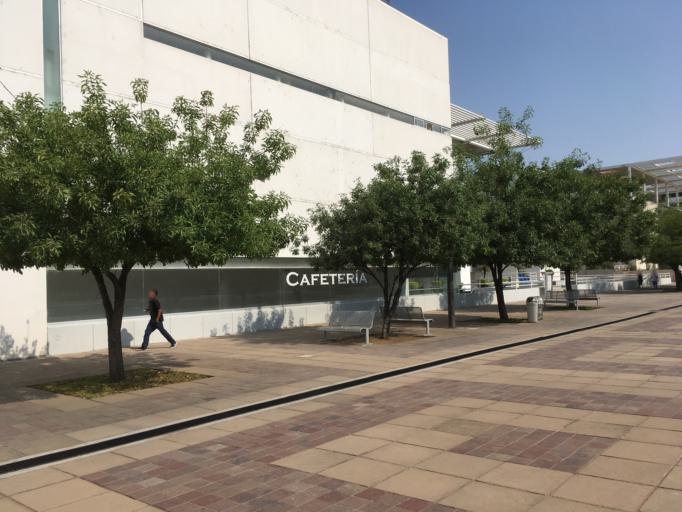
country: MX
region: Guanajuato
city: Leon
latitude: 21.1156
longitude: -101.6606
